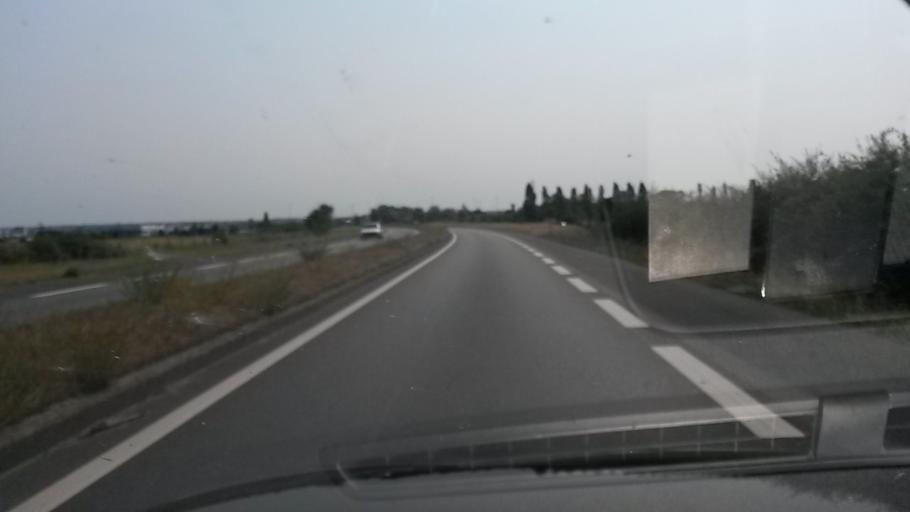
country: FR
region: Pays de la Loire
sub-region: Departement de la Loire-Atlantique
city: Saint-Gereon
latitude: 47.4054
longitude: -1.1908
